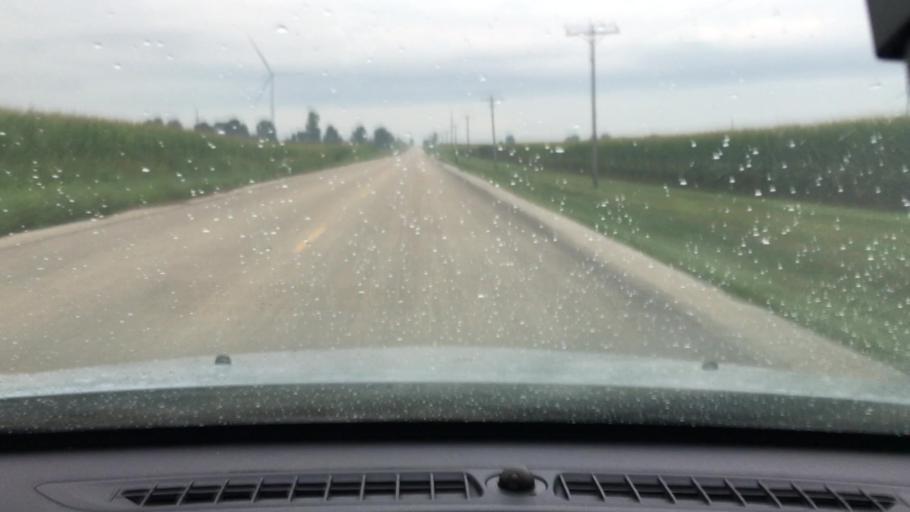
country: US
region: Illinois
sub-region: DeKalb County
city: Waterman
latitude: 41.8328
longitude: -88.7733
